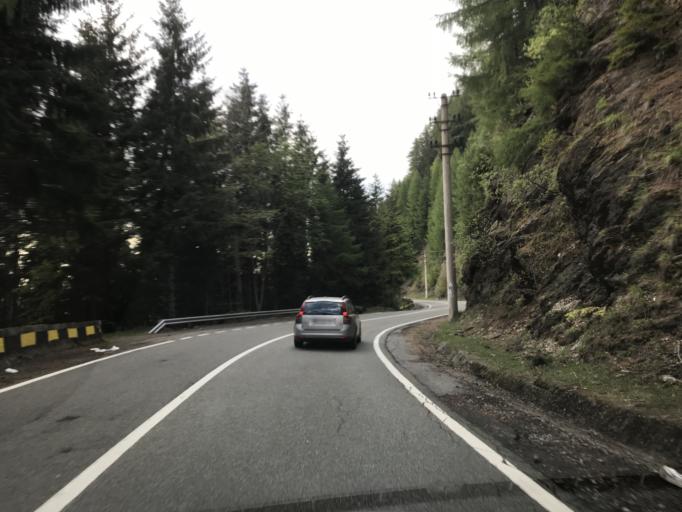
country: RO
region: Sibiu
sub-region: Comuna Cartisoara
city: Cartisoara
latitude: 45.6561
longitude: 24.6020
